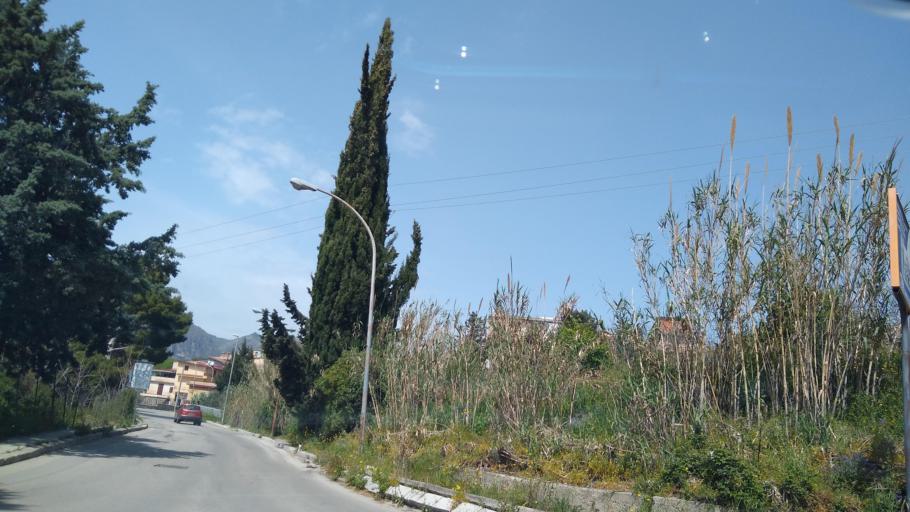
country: IT
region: Sicily
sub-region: Palermo
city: San Cipirello
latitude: 37.9666
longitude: 13.1784
